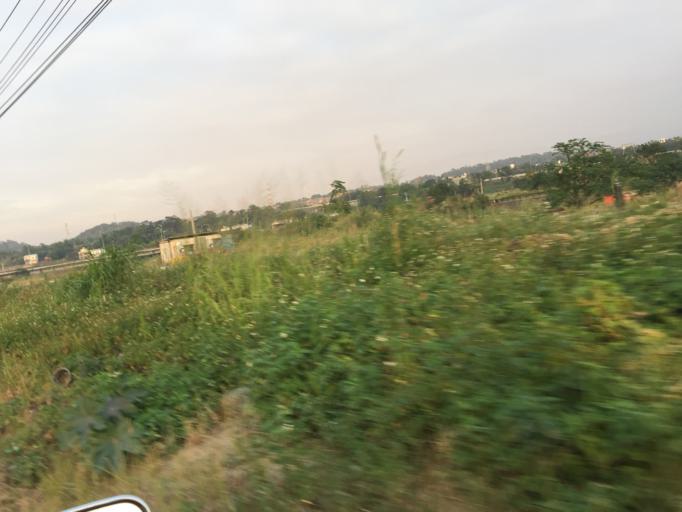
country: TW
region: Taiwan
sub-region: Miaoli
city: Miaoli
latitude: 24.4927
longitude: 120.7784
